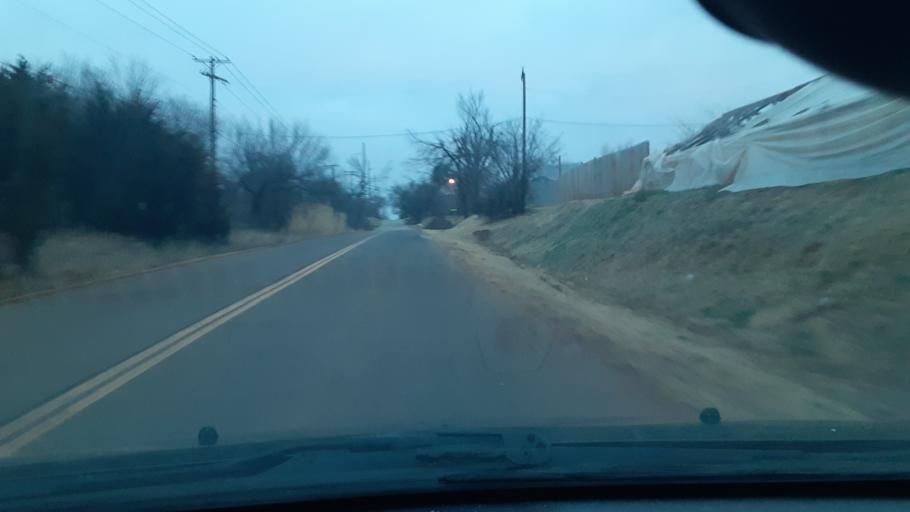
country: US
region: Oklahoma
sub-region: Logan County
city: Guthrie
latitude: 35.8697
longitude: -97.4075
